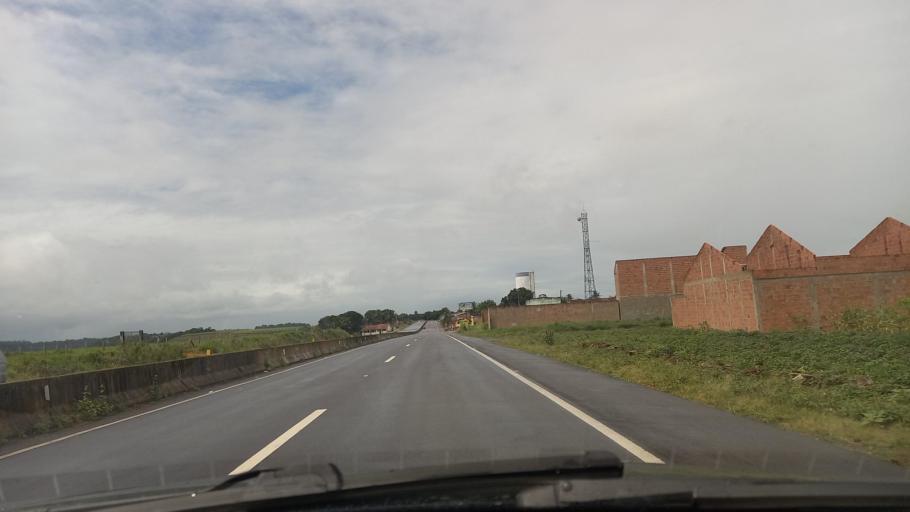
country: BR
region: Alagoas
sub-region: Campo Alegre
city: Campo Alegre
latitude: -9.8017
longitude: -36.2777
